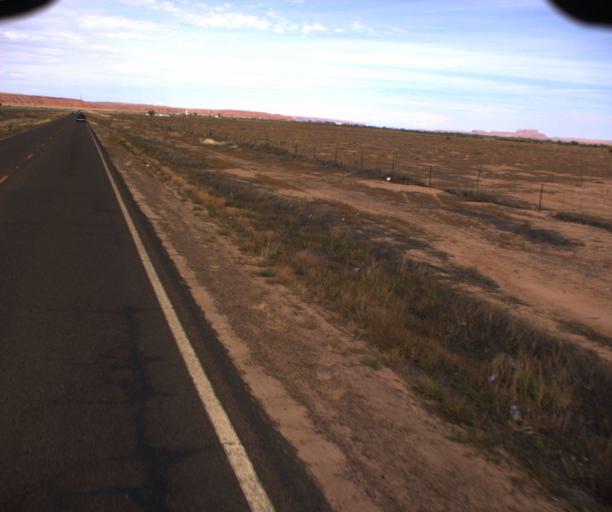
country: US
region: Arizona
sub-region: Apache County
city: Many Farms
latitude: 36.3207
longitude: -109.6163
